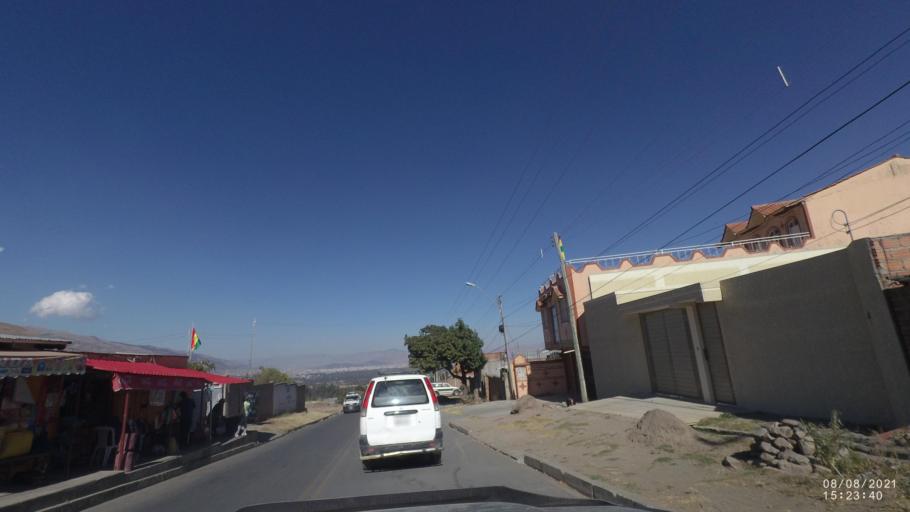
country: BO
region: Cochabamba
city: Cochabamba
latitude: -17.3102
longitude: -66.2923
